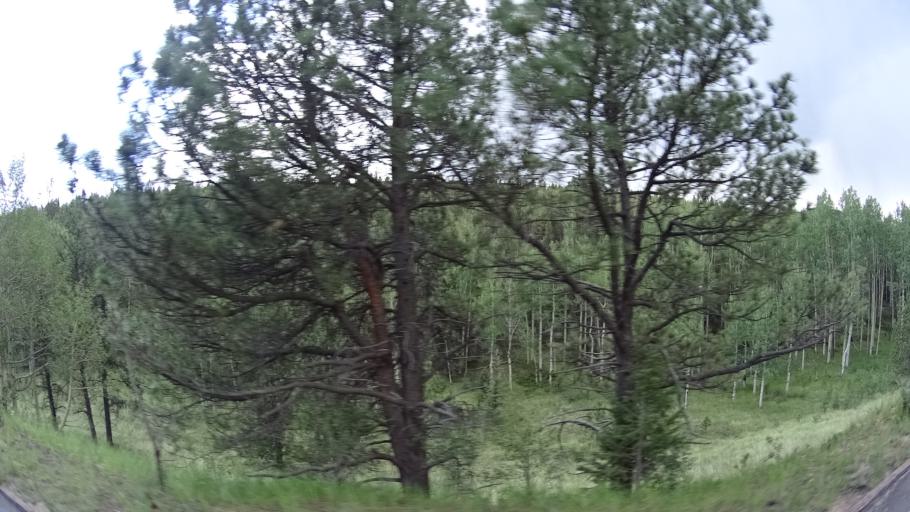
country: US
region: Colorado
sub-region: El Paso County
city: Cascade-Chipita Park
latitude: 38.9118
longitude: -105.0237
